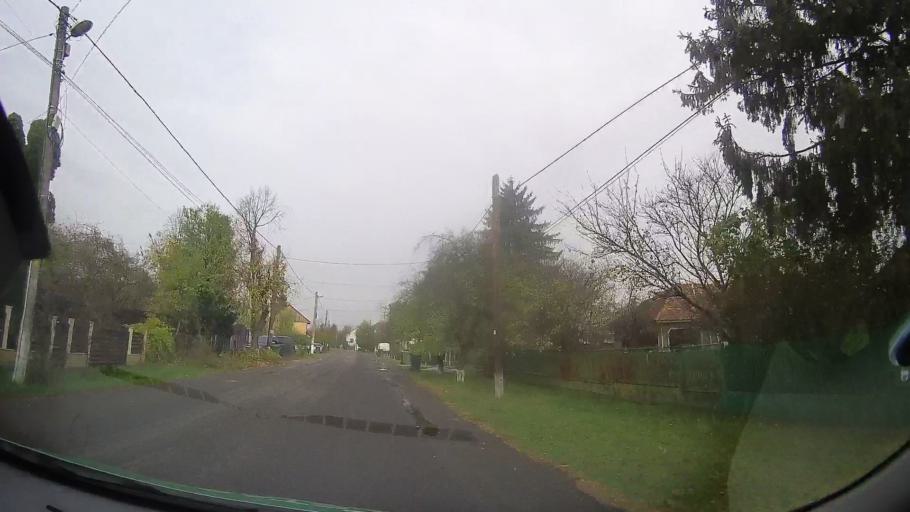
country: RO
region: Ilfov
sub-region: Comuna Snagov
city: Snagov
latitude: 44.7111
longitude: 26.1726
